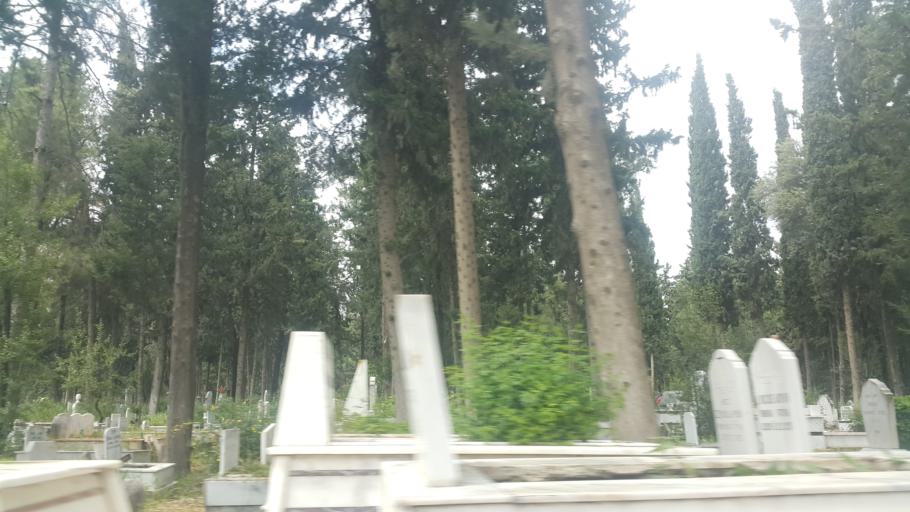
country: TR
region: Mersin
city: Mercin
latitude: 36.8174
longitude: 34.6056
